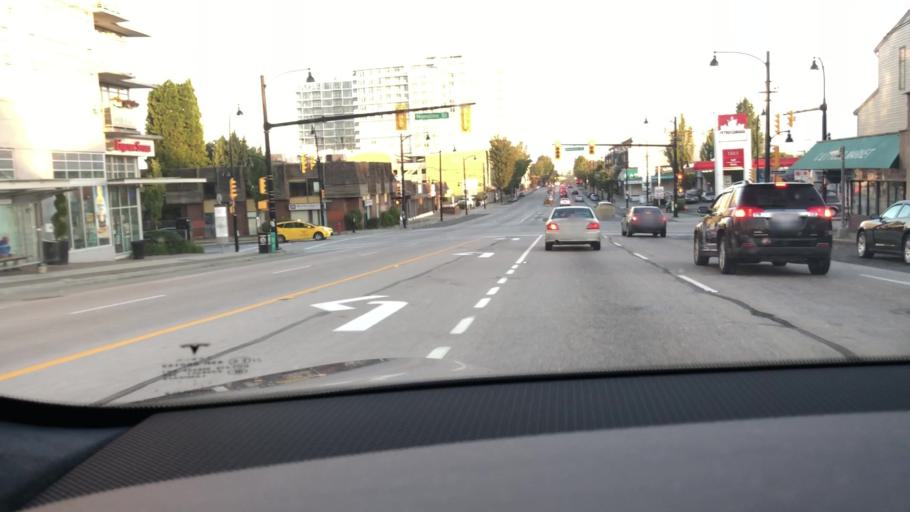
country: CA
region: British Columbia
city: Vancouver
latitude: 49.2417
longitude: -123.0575
